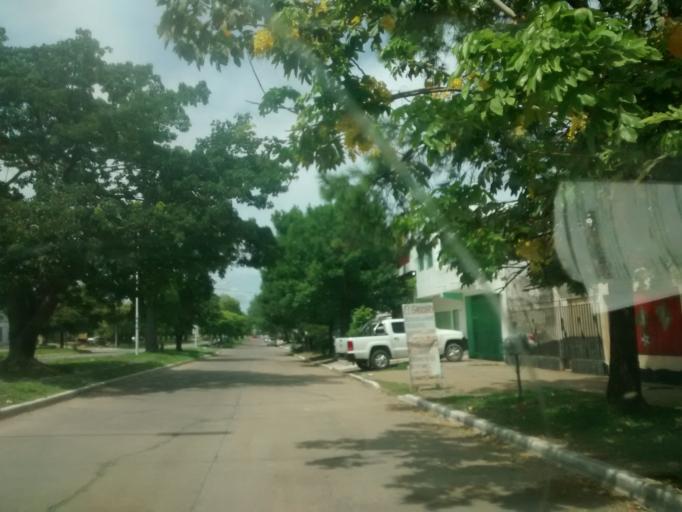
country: AR
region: Chaco
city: Resistencia
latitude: -27.4488
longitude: -58.9984
